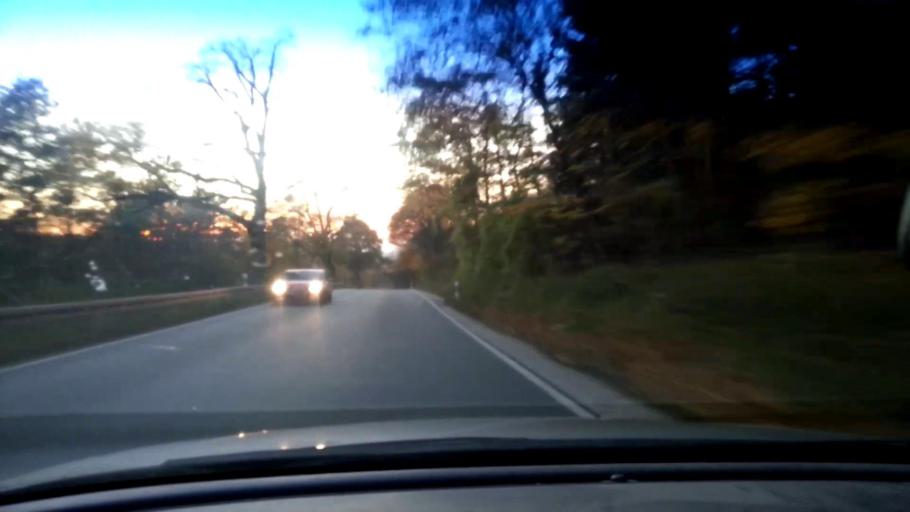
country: DE
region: Bavaria
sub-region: Upper Franconia
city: Poxdorf
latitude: 49.8693
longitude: 11.0825
